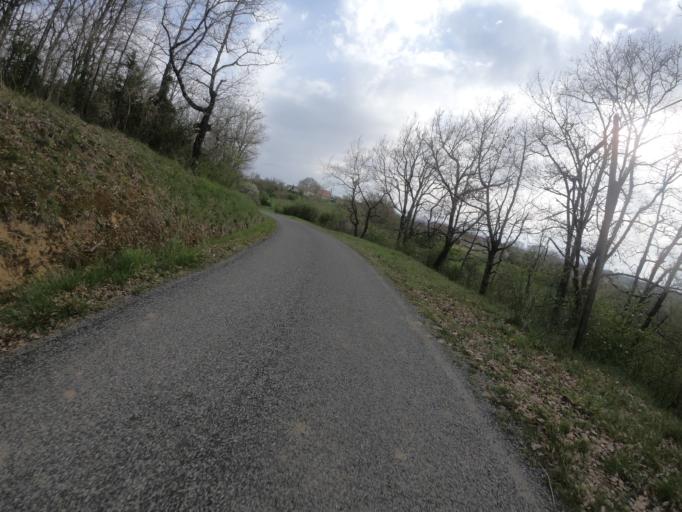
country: FR
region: Languedoc-Roussillon
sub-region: Departement de l'Aude
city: Belpech
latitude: 43.1259
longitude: 1.7424
